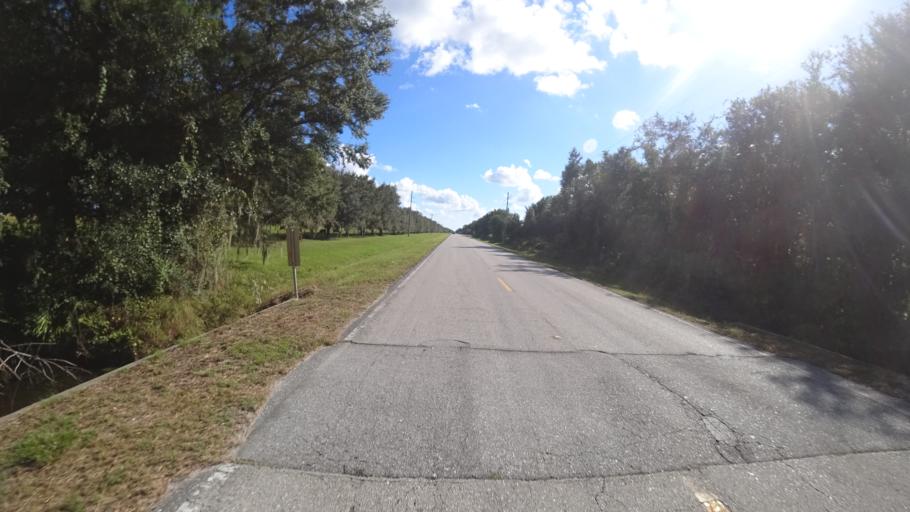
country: US
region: Florida
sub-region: Sarasota County
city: The Meadows
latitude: 27.4227
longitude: -82.3037
